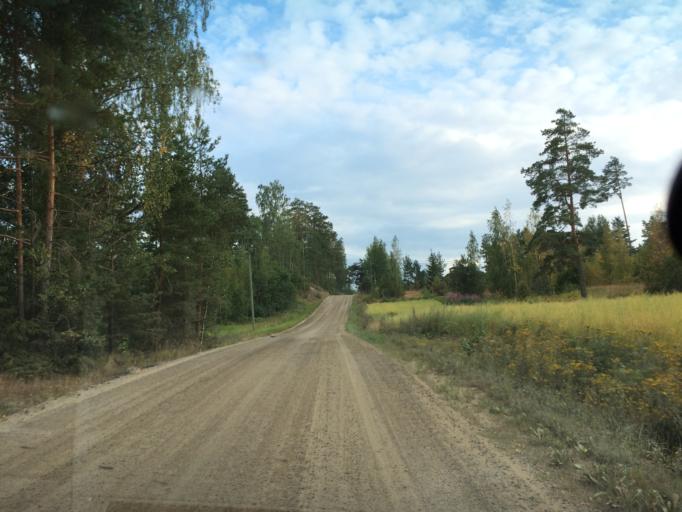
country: FI
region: Pirkanmaa
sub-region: Tampere
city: Luopioinen
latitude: 61.2603
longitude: 24.7068
